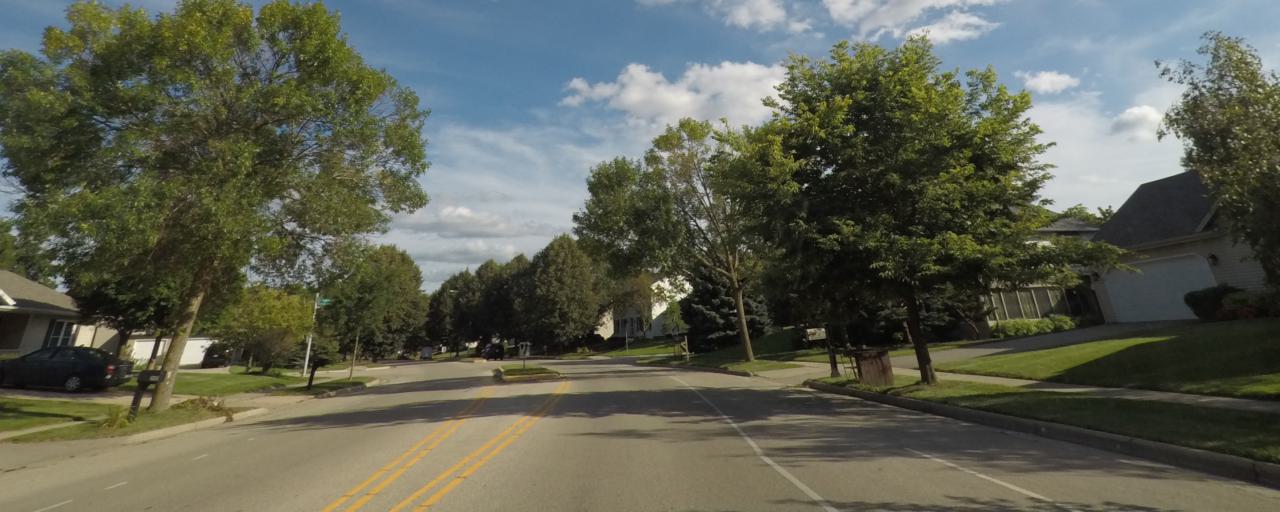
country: US
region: Wisconsin
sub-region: Dane County
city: Middleton
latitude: 43.0703
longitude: -89.5202
